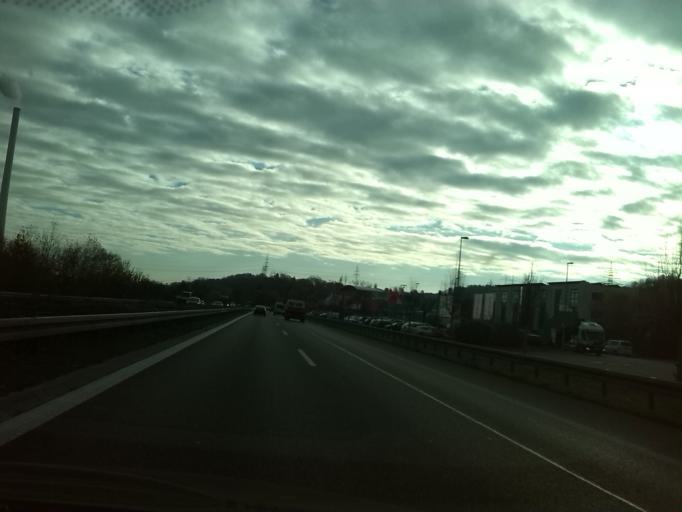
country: DE
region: Baden-Wuerttemberg
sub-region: Regierungsbezirk Stuttgart
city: Altbach
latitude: 48.7175
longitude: 9.3533
